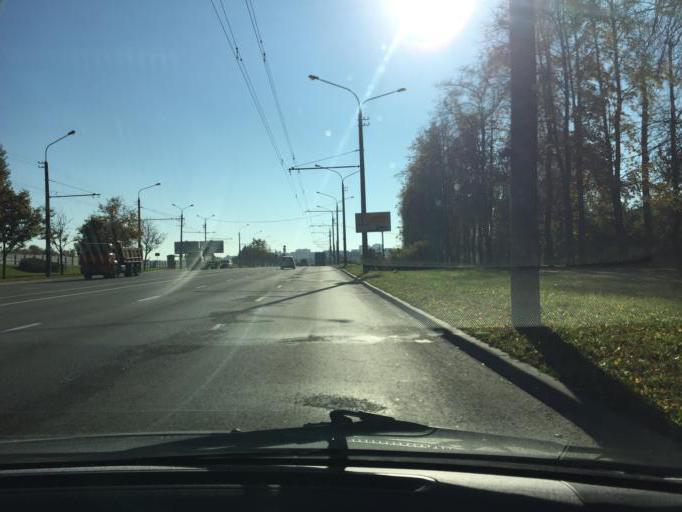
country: BY
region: Minsk
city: Syenitsa
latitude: 53.8635
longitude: 27.5323
